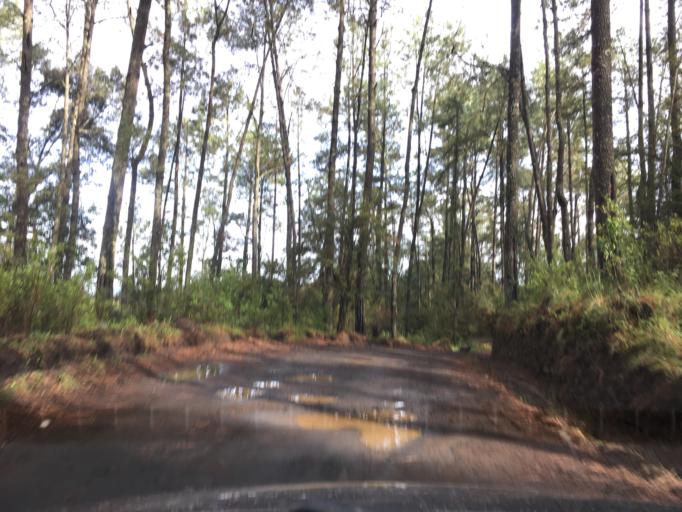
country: MX
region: Michoacan
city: Angahuan
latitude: 19.5181
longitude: -102.2205
